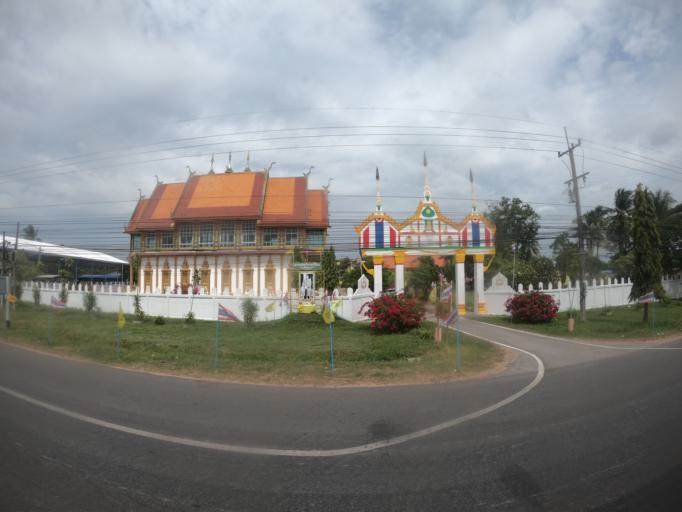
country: TH
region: Roi Et
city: Roi Et
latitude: 16.0667
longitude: 103.6112
